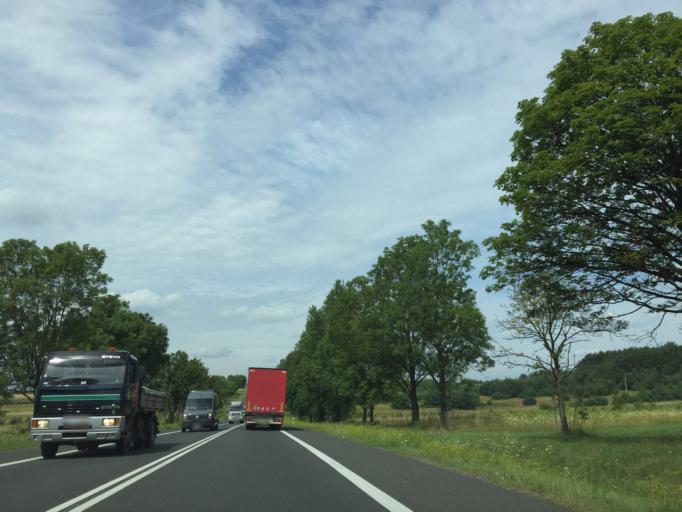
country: PL
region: Lesser Poland Voivodeship
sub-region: Powiat krakowski
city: Przeginia
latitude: 50.2527
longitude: 19.6527
